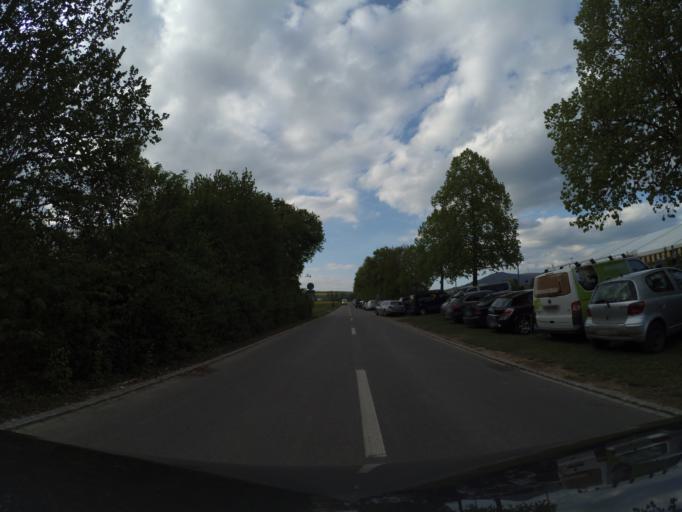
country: CH
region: Schaffhausen
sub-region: Bezirk Oberklettgau
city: Neunkirch
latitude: 47.6914
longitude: 8.4976
